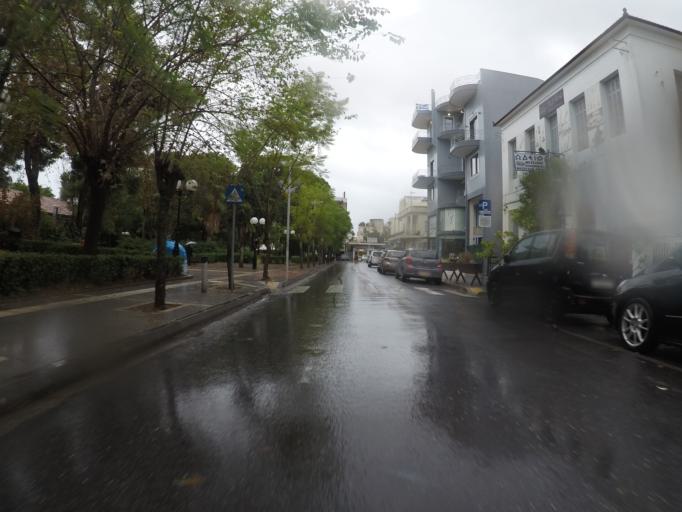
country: GR
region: Peloponnese
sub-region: Nomos Messinias
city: Messini
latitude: 37.0516
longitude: 22.0074
